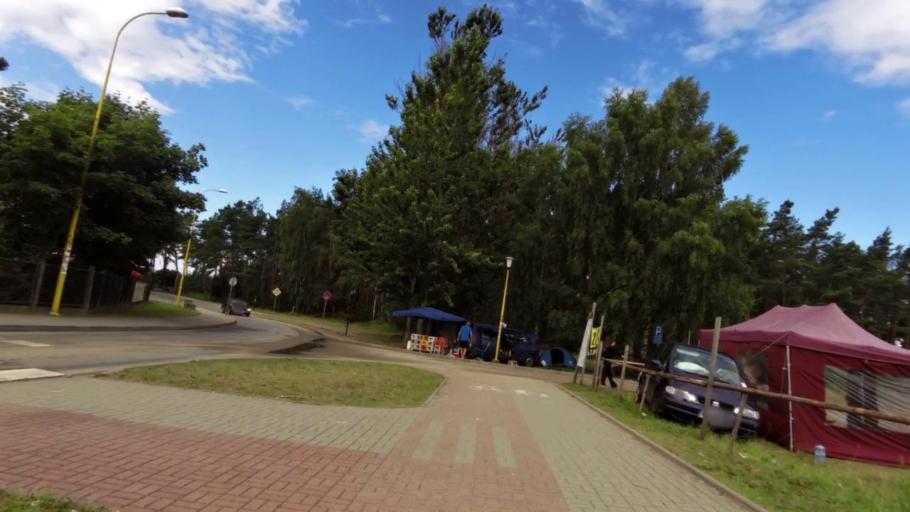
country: PL
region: West Pomeranian Voivodeship
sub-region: Powiat slawienski
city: Darlowo
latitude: 54.4448
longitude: 16.3945
